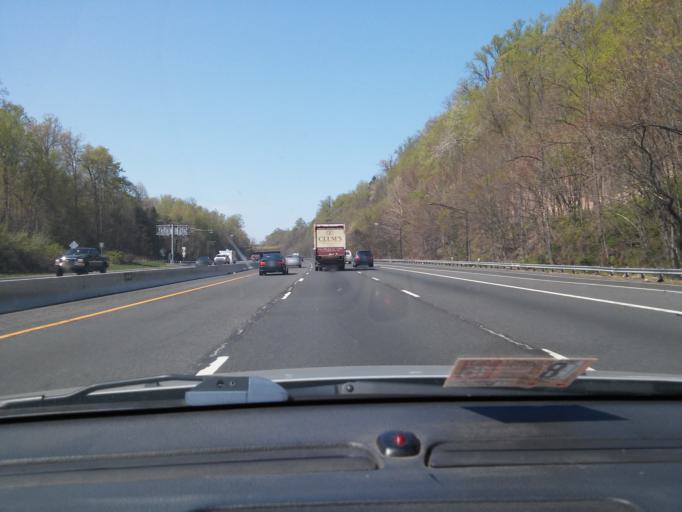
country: US
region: New Jersey
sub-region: Union County
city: Mountainside
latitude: 40.6975
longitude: -74.3679
